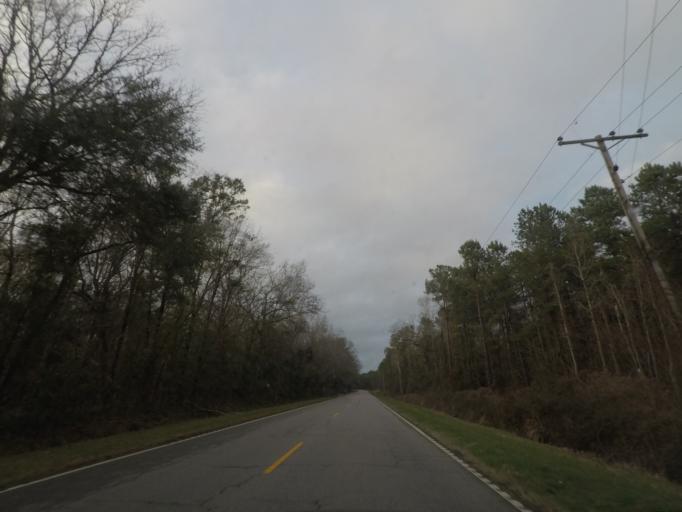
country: US
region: South Carolina
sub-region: Dorchester County
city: Saint George
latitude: 33.0657
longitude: -80.6314
